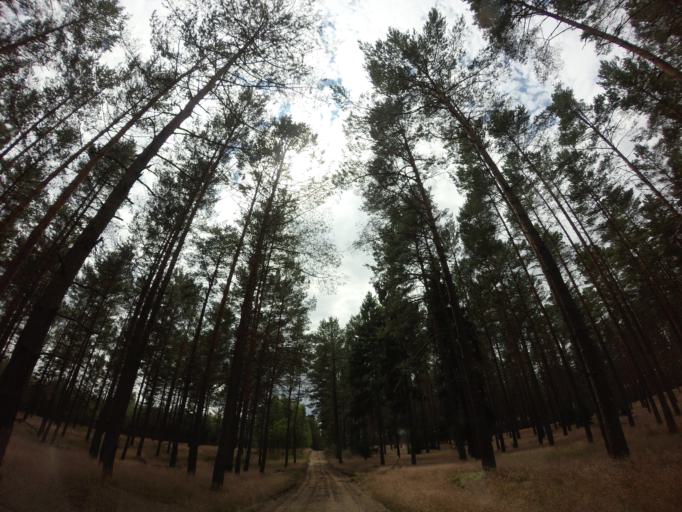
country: PL
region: West Pomeranian Voivodeship
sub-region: Powiat choszczenski
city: Drawno
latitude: 53.1569
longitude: 15.7674
